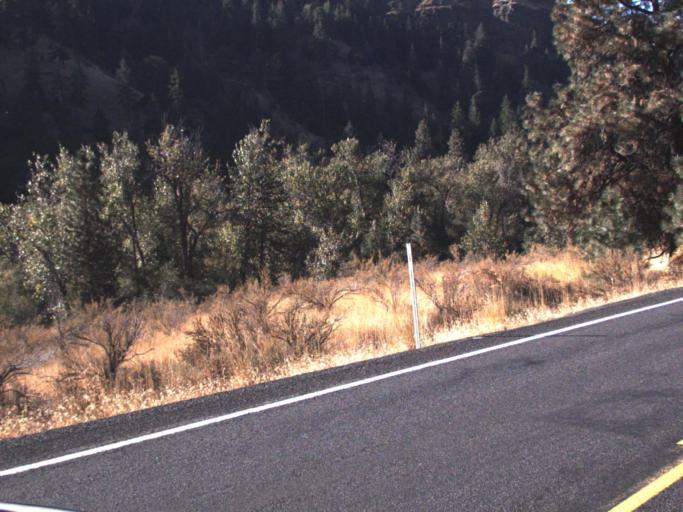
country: US
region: Washington
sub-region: Yakima County
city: Tieton
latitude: 46.7126
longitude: -120.8727
